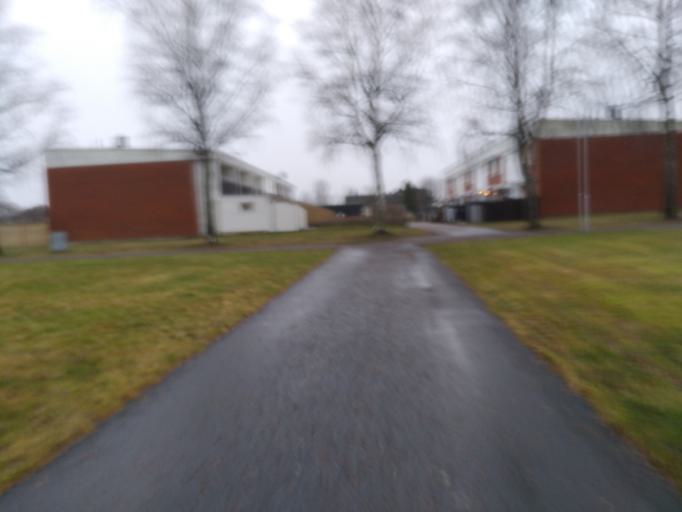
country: SE
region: Vaestra Goetaland
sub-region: Lidkopings Kommun
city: Lidkoping
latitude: 58.4877
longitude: 13.1458
